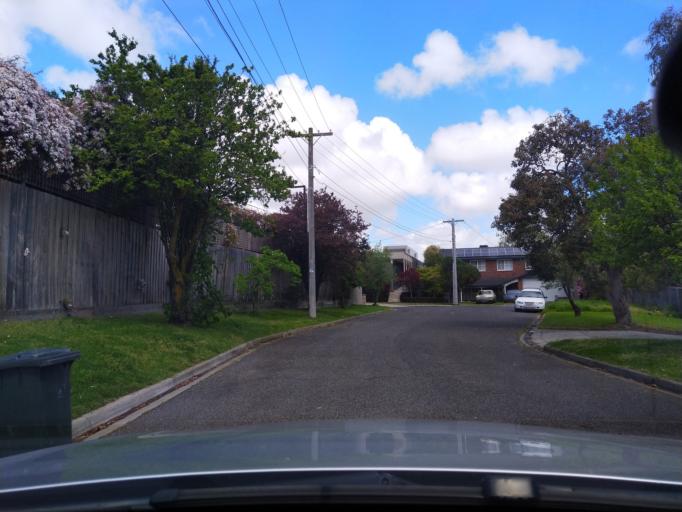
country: AU
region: Victoria
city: Rosanna
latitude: -37.7642
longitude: 145.0590
